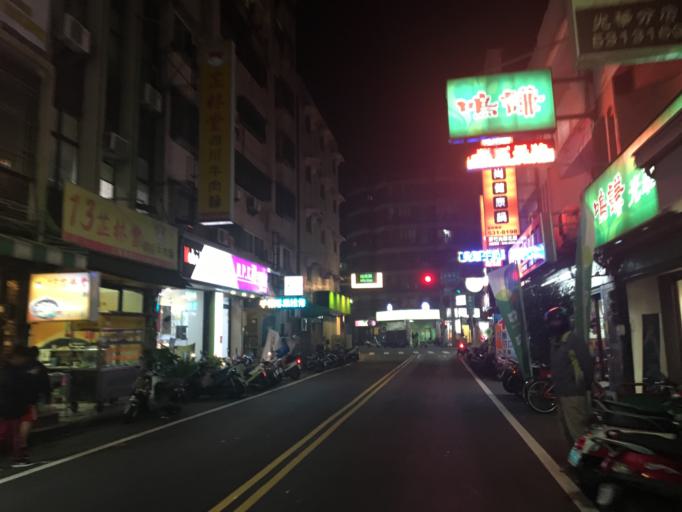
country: TW
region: Taiwan
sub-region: Hsinchu
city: Hsinchu
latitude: 24.8178
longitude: 120.9728
